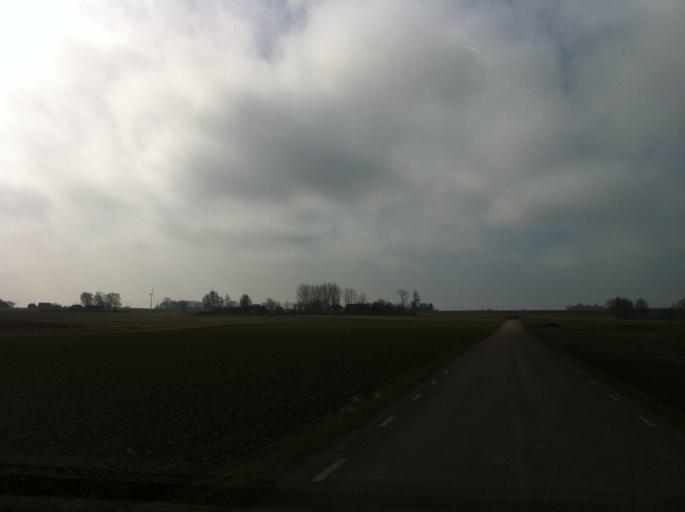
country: SE
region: Skane
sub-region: Svalovs Kommun
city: Teckomatorp
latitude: 55.8647
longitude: 13.0636
